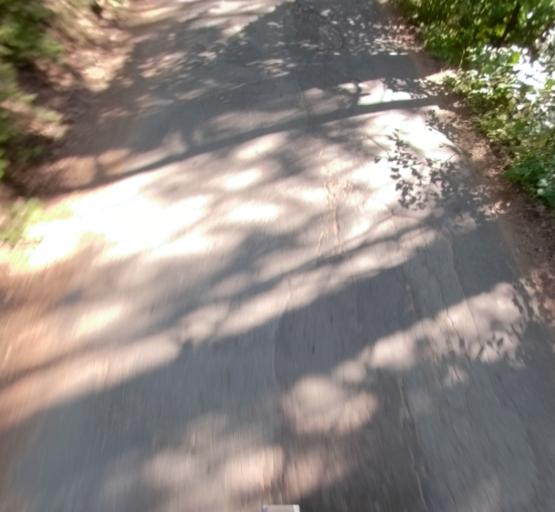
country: US
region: California
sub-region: Madera County
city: Oakhurst
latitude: 37.4364
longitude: -119.6374
